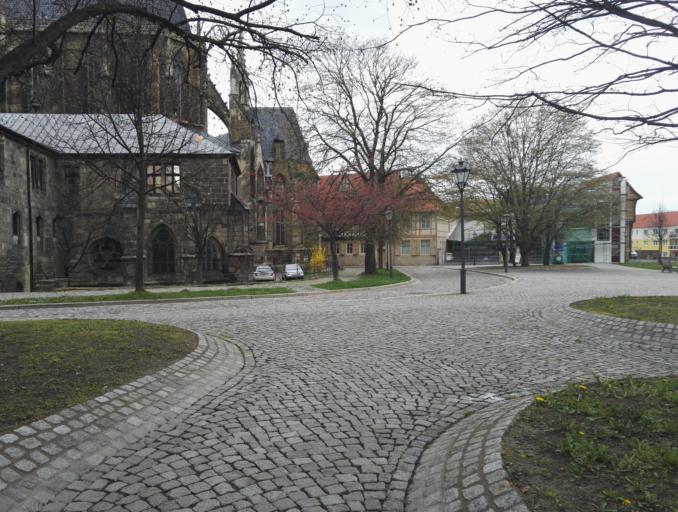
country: DE
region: Saxony-Anhalt
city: Halberstadt
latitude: 51.8958
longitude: 11.0498
